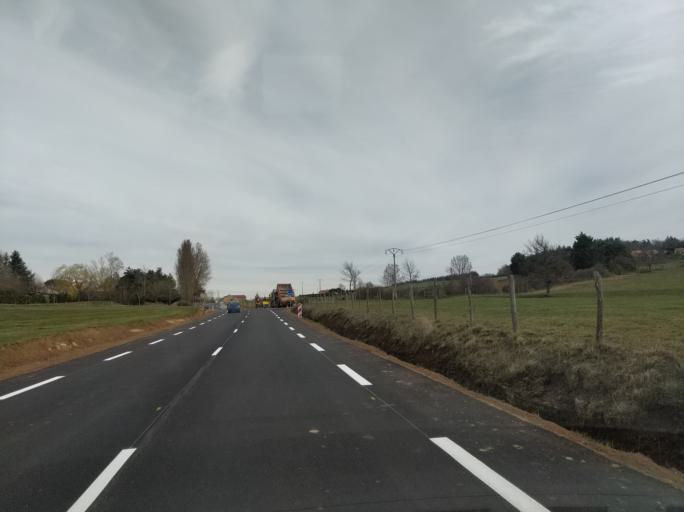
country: FR
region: Rhone-Alpes
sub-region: Departement de l'Ardeche
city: Satillieu
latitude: 45.1742
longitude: 4.6425
